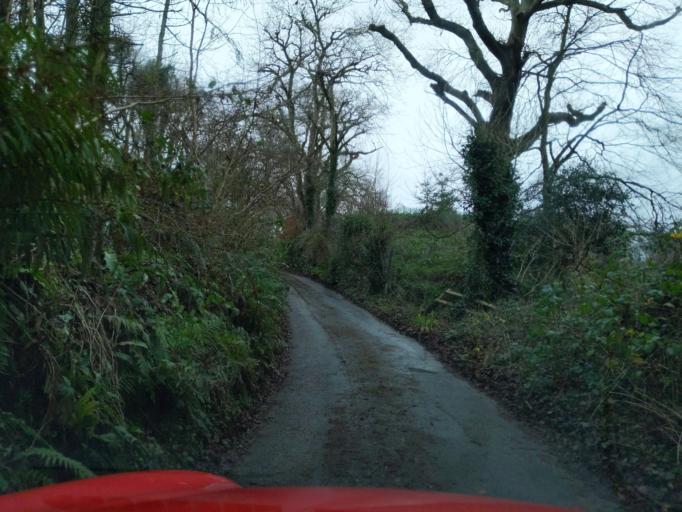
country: GB
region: England
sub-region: Cornwall
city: Duloe
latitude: 50.3462
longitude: -4.5230
